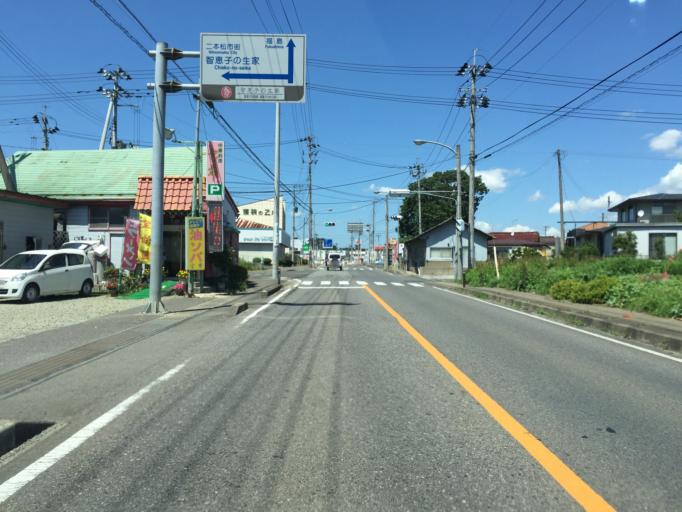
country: JP
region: Fukushima
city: Nihommatsu
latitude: 37.6029
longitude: 140.4609
